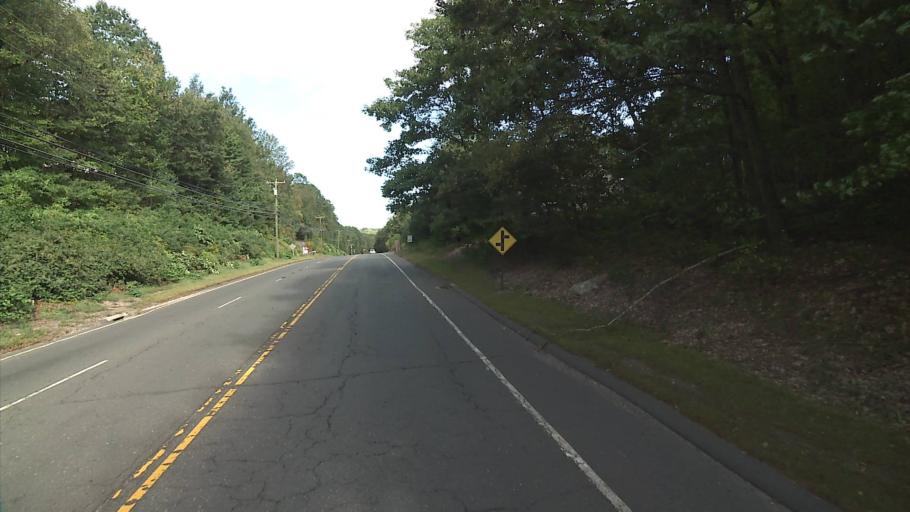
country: US
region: Connecticut
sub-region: Hartford County
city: Bristol
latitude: 41.6501
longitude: -72.9648
